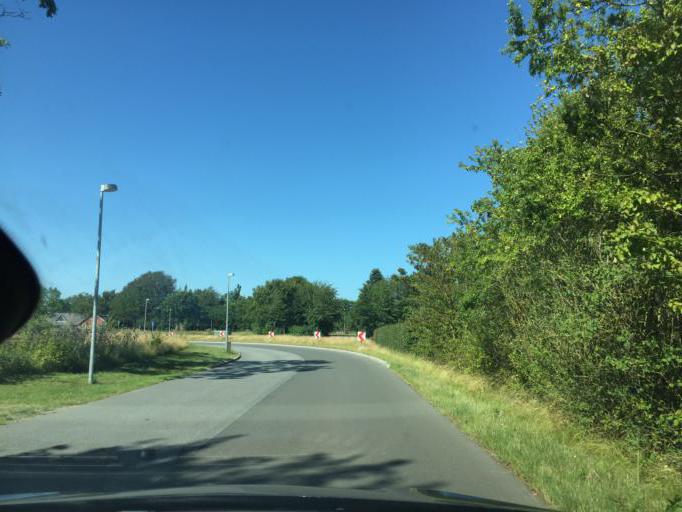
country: DK
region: South Denmark
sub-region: Nordfyns Kommune
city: Sonderso
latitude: 55.4960
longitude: 10.2662
